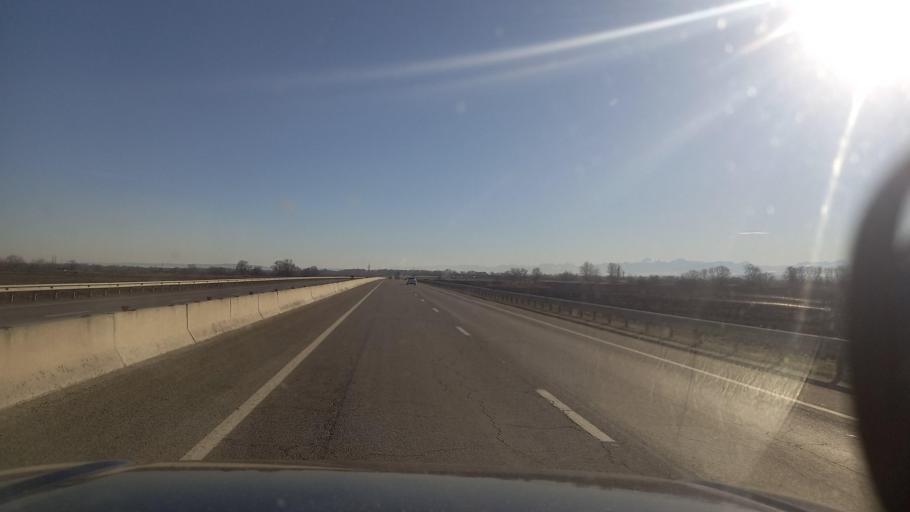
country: RU
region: Kabardino-Balkariya
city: Germenchik
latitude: 43.5778
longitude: 43.7015
